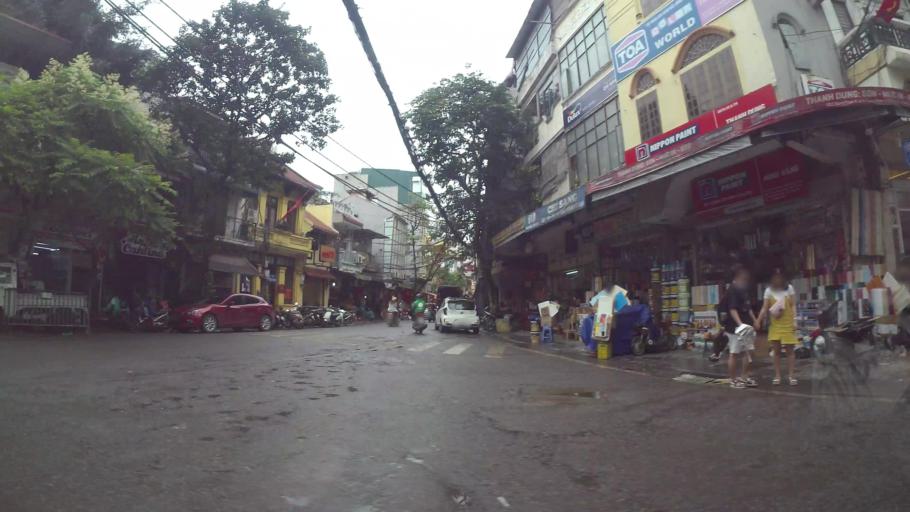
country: VN
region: Ha Noi
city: Hoan Kiem
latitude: 21.0326
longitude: 105.8484
